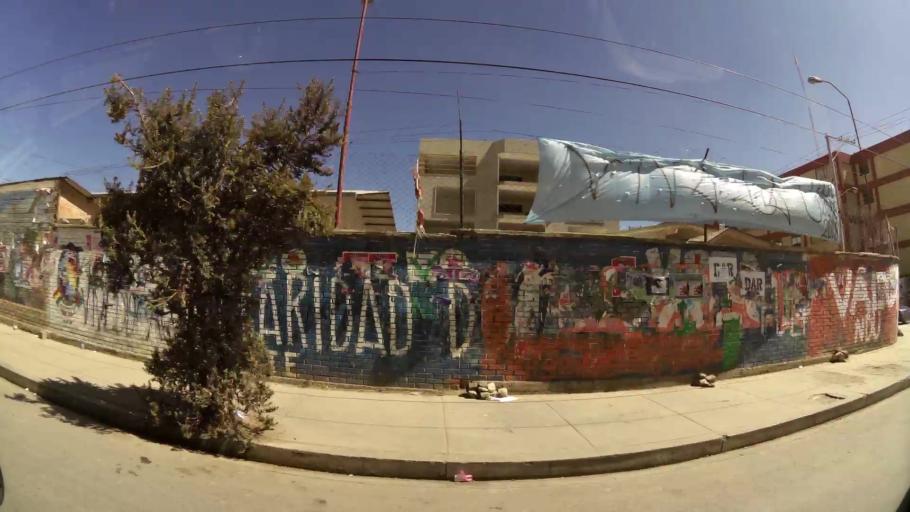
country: BO
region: La Paz
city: La Paz
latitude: -16.4923
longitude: -68.1934
